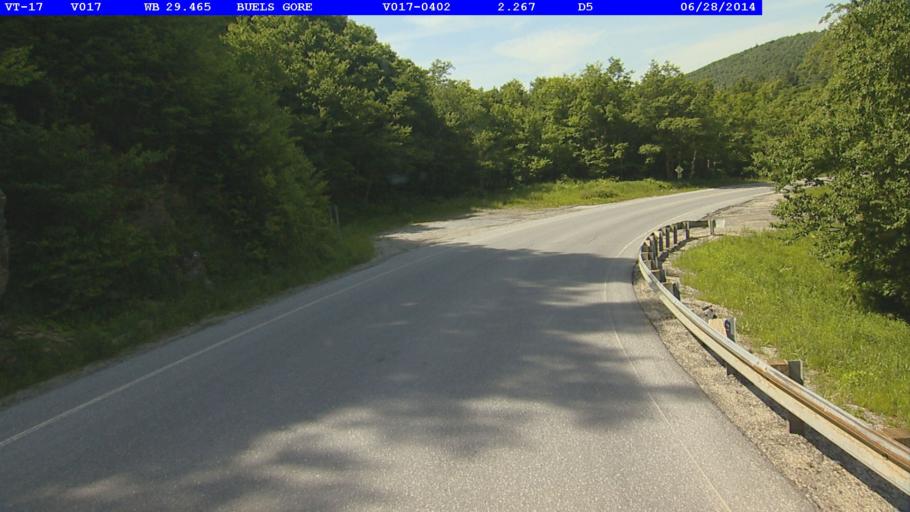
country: US
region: Vermont
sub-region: Addison County
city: Bristol
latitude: 44.2117
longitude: -72.9358
